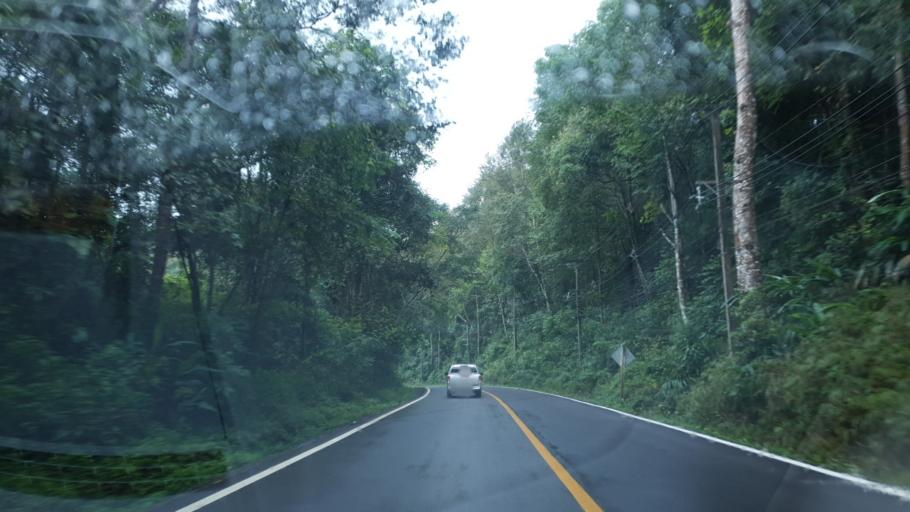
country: TH
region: Mae Hong Son
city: Ban Huai I Huak
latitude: 18.1422
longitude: 98.0899
